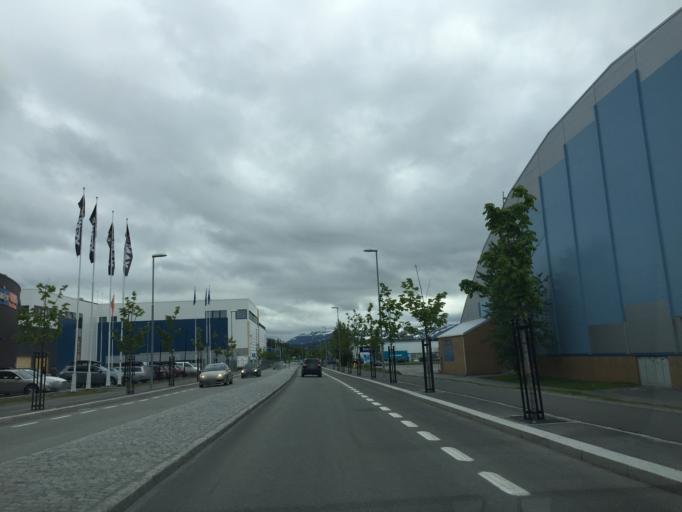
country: NO
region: Nordland
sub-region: Bodo
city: Bodo
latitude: 67.2790
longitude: 14.4169
